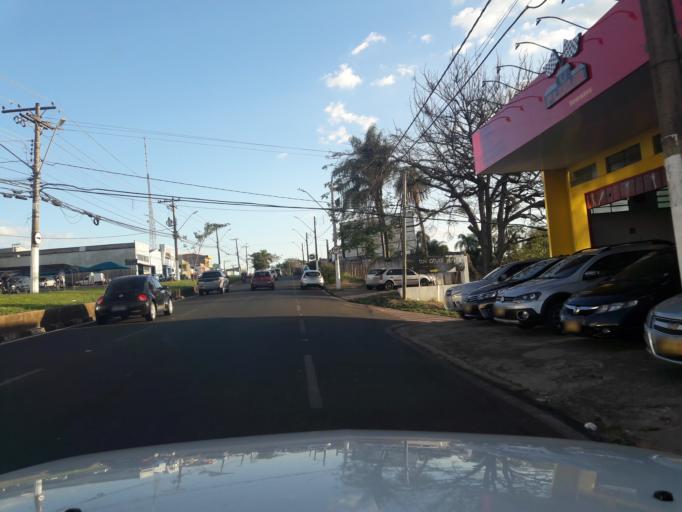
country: BR
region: Sao Paulo
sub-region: Moji-Guacu
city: Mogi-Gaucu
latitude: -22.3956
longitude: -46.9470
